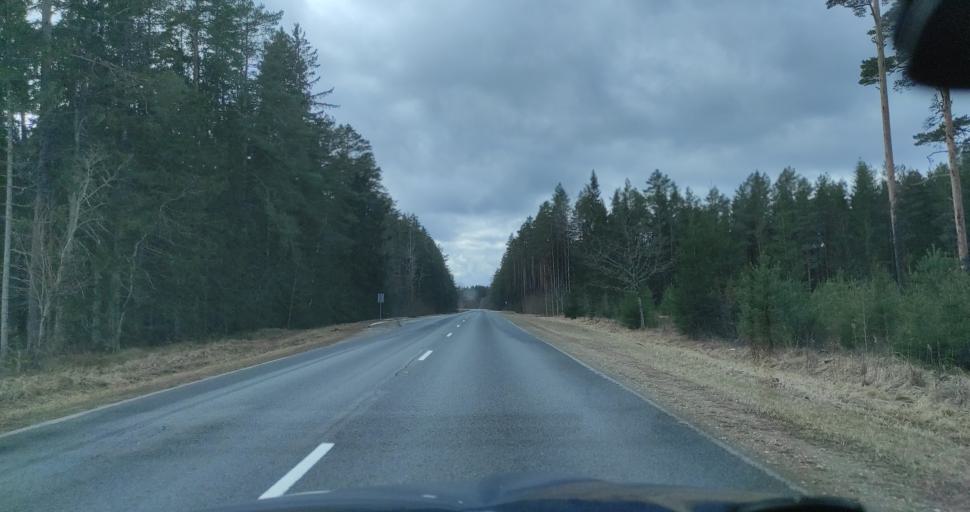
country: LV
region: Talsu Rajons
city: Stende
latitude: 57.1085
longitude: 22.4958
